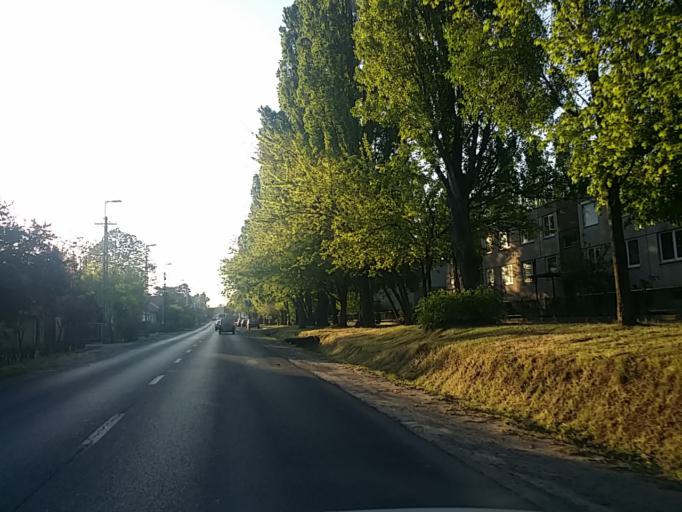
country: HU
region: Pest
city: Dunakeszi
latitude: 47.6276
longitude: 19.1483
